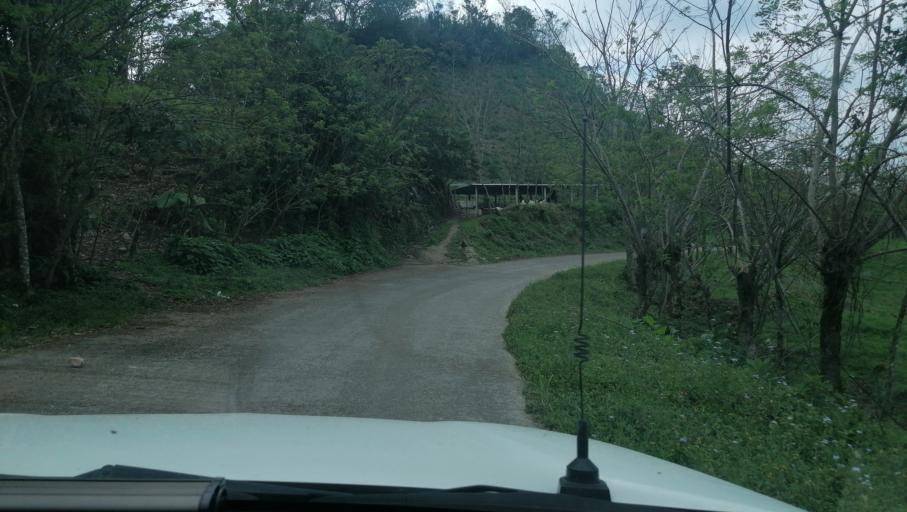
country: MX
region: Chiapas
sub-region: Francisco Leon
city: San Miguel la Sardina
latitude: 17.2372
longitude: -93.3140
